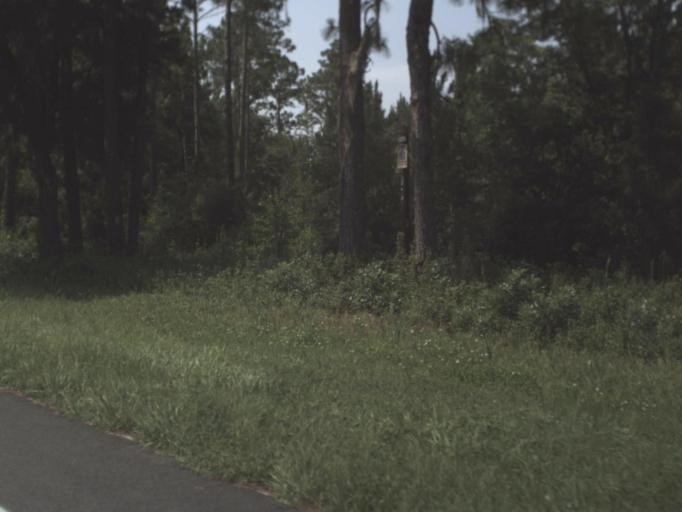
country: US
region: Florida
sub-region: Hamilton County
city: Jasper
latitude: 30.5794
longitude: -82.9979
